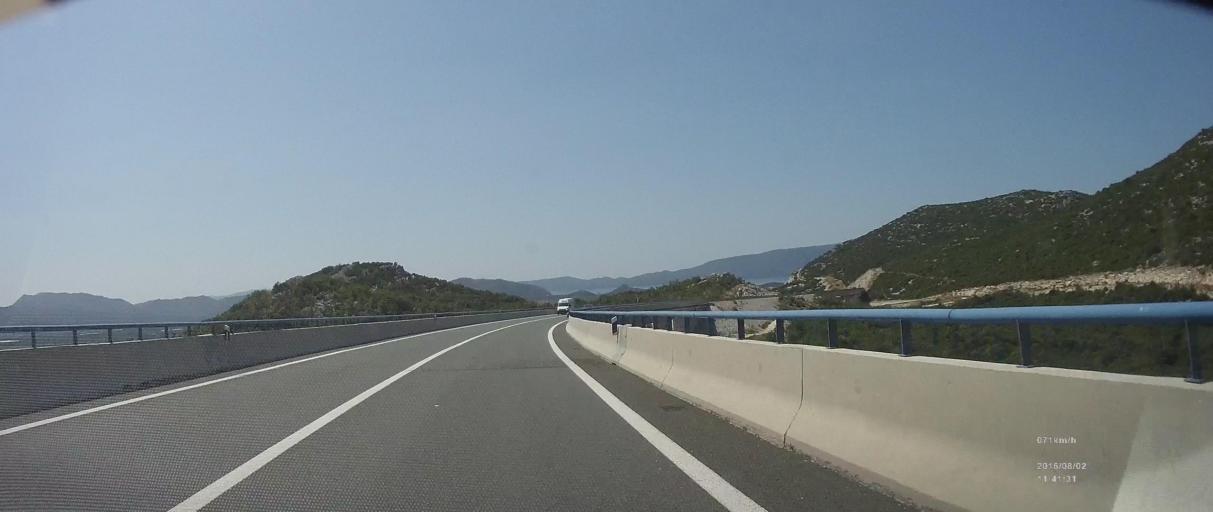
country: HR
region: Dubrovacko-Neretvanska
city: Komin
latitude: 43.0627
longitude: 17.4958
